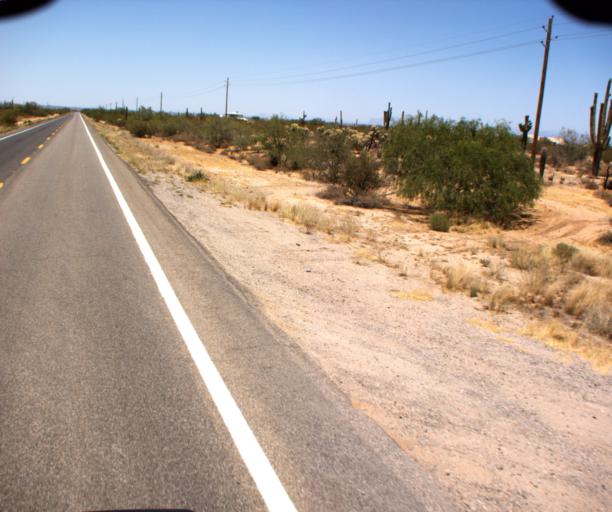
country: US
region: Arizona
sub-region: Pinal County
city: Florence
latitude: 32.9670
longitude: -111.3417
